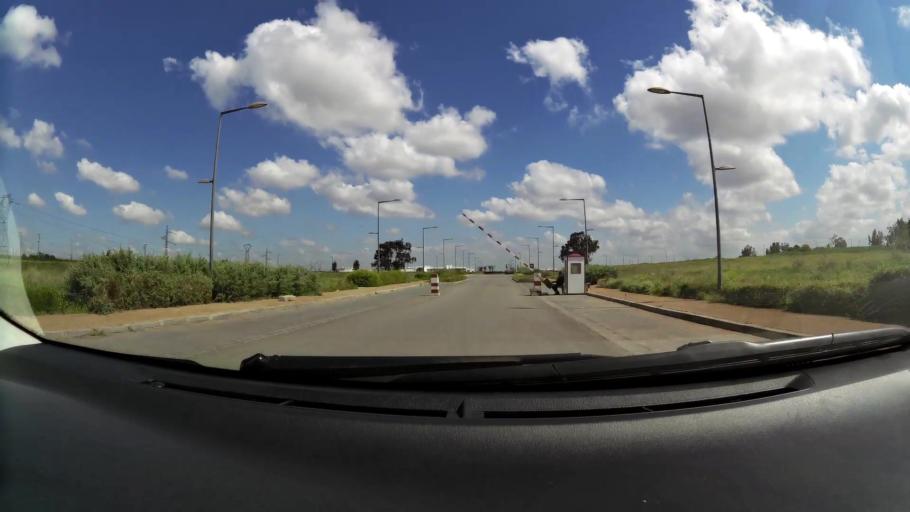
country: MA
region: Grand Casablanca
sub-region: Nouaceur
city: Bouskoura
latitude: 33.4976
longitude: -7.6076
